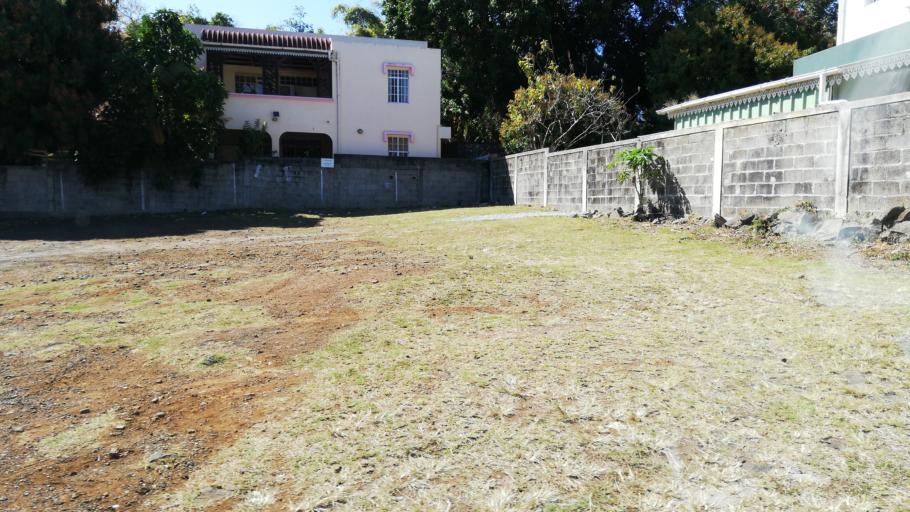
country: MU
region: Plaines Wilhems
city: Ebene
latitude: -20.2306
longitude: 57.4742
